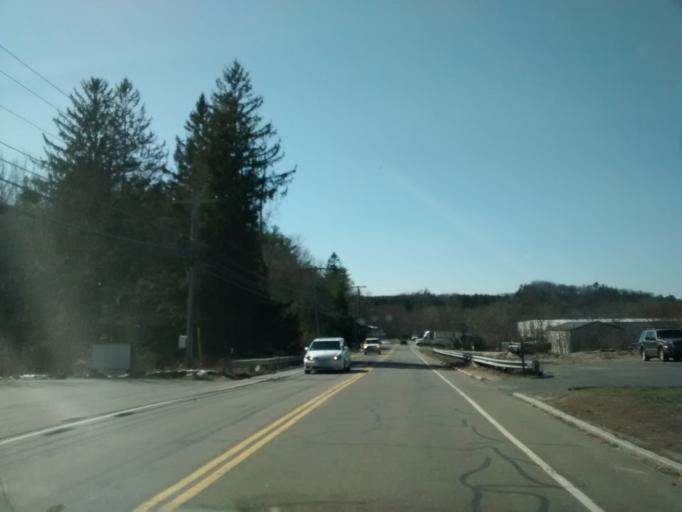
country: US
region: Massachusetts
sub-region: Worcester County
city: Millbury
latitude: 42.1748
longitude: -71.7236
